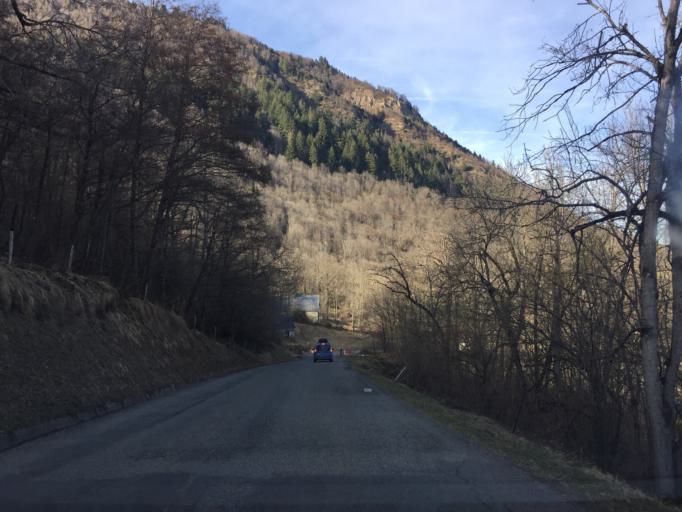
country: FR
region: Midi-Pyrenees
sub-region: Departement des Hautes-Pyrenees
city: Saint-Lary-Soulan
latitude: 42.8054
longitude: 0.4004
